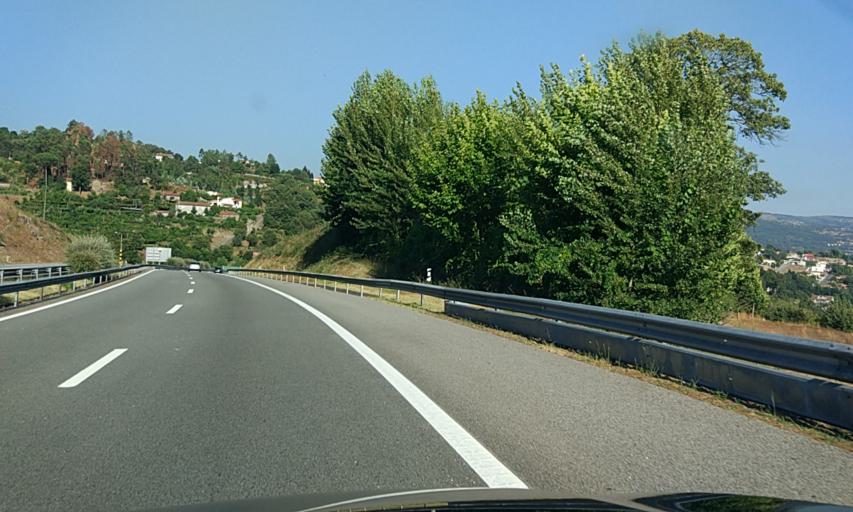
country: PT
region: Porto
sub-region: Marco de Canaveses
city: Marco de Canavezes
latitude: 41.2275
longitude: -8.1622
